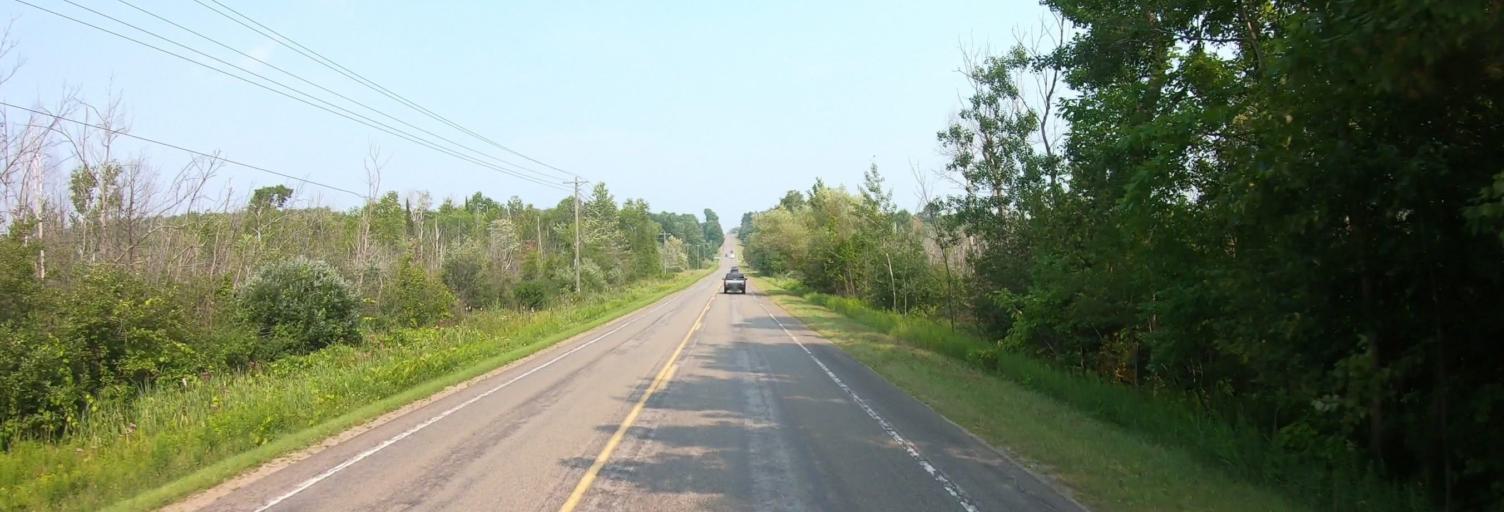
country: US
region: Michigan
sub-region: Charlevoix County
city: Charlevoix
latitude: 45.1854
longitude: -85.3162
